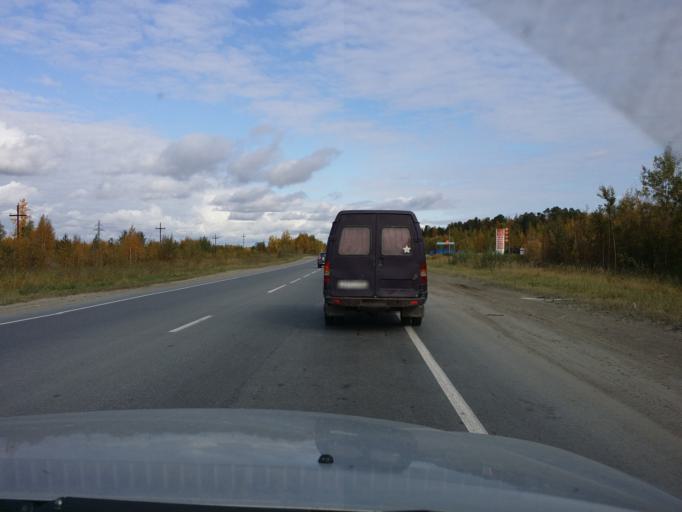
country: RU
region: Khanty-Mansiyskiy Avtonomnyy Okrug
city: Megion
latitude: 61.0598
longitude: 76.1144
